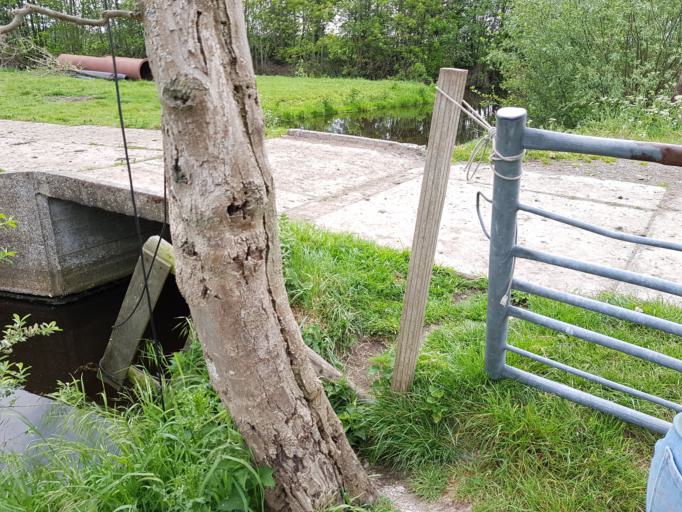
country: NL
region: South Holland
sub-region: Gemeente Vlist
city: Haastrecht
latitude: 51.9991
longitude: 4.7504
